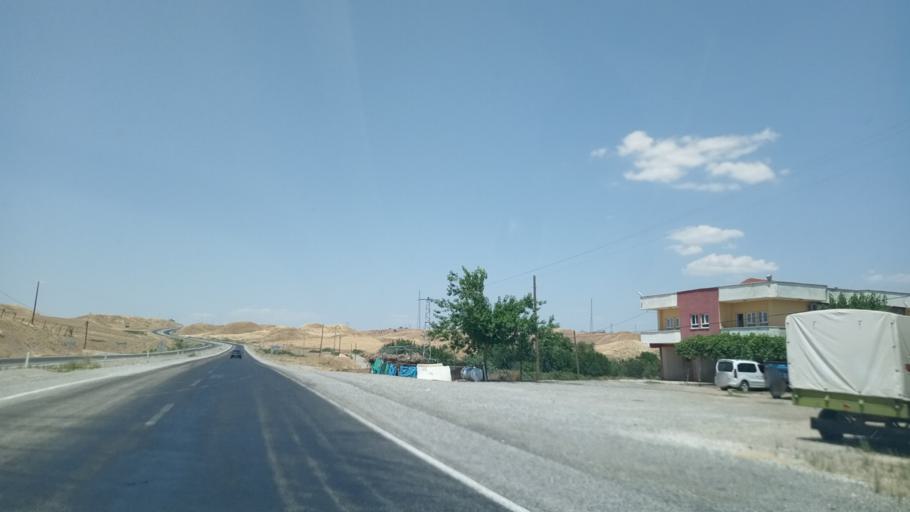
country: TR
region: Batman
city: Bekirhan
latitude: 38.1510
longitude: 41.3888
